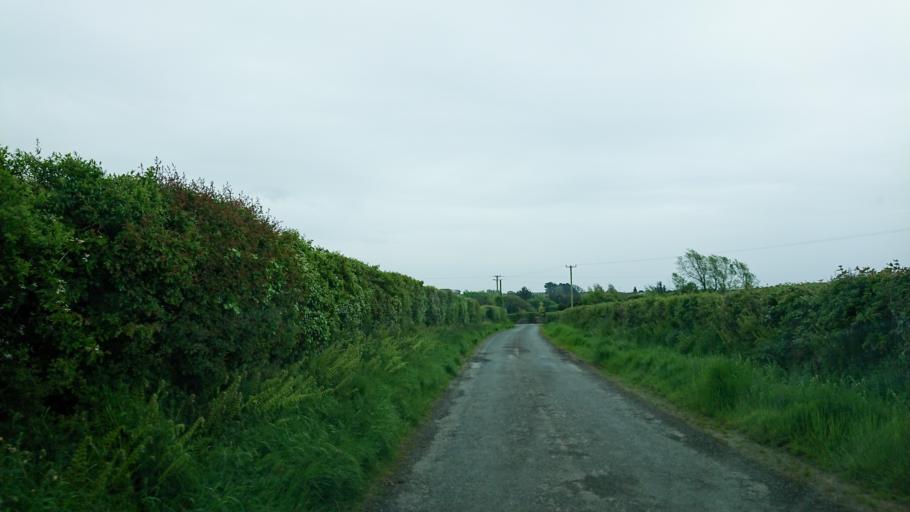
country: IE
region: Munster
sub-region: Waterford
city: Dunmore East
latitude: 52.2233
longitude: -7.0188
